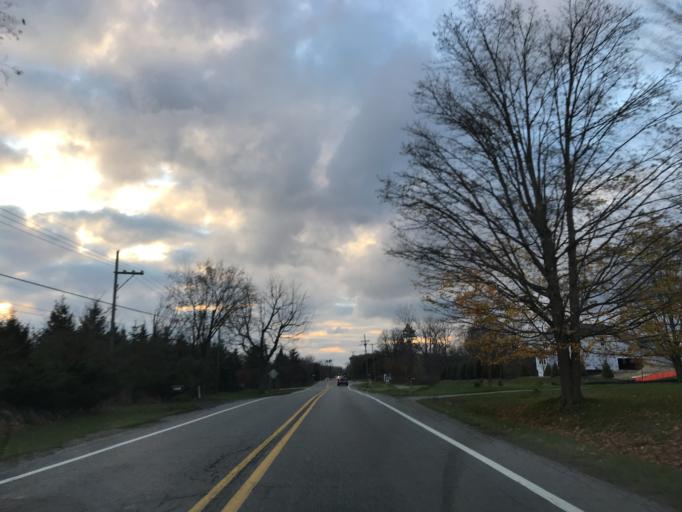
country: US
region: Michigan
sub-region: Oakland County
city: South Lyon
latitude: 42.4616
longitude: -83.6247
